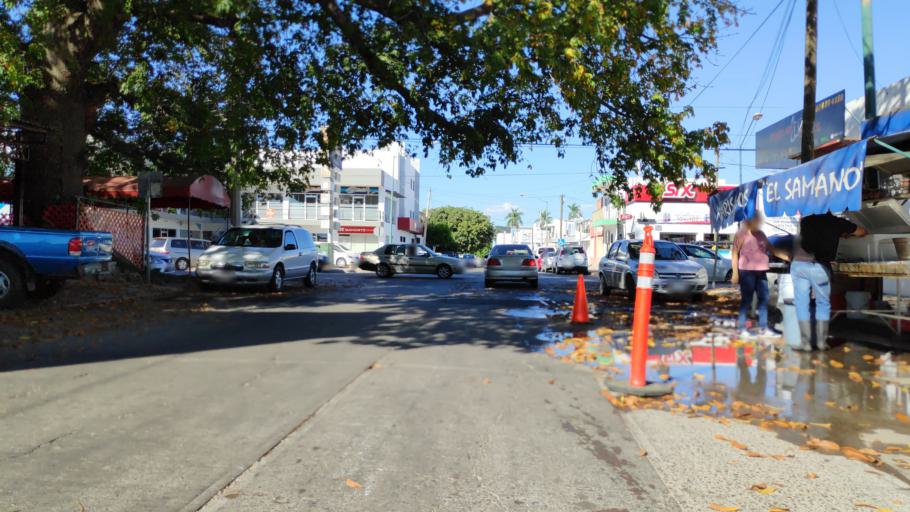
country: MX
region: Sinaloa
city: Culiacan
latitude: 24.7998
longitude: -107.3965
